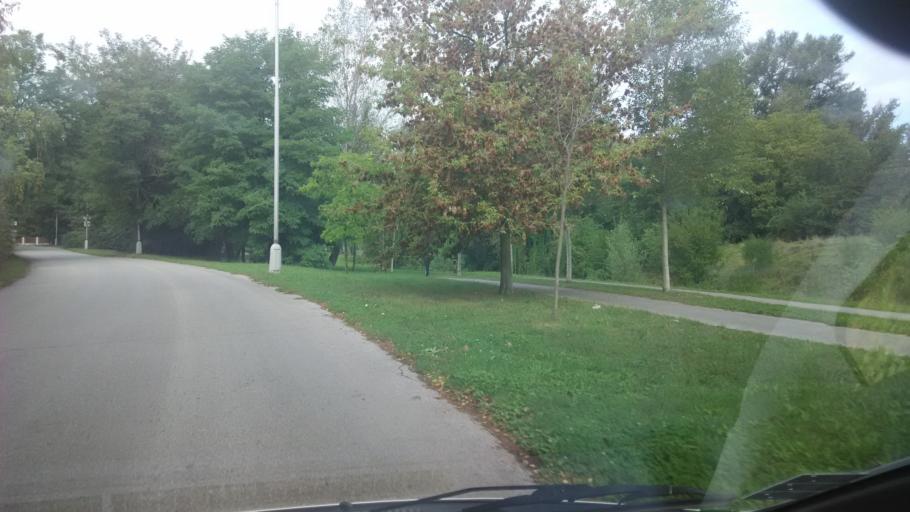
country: SK
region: Trnavsky
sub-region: Okres Trnava
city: Piestany
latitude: 48.5738
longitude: 17.8208
